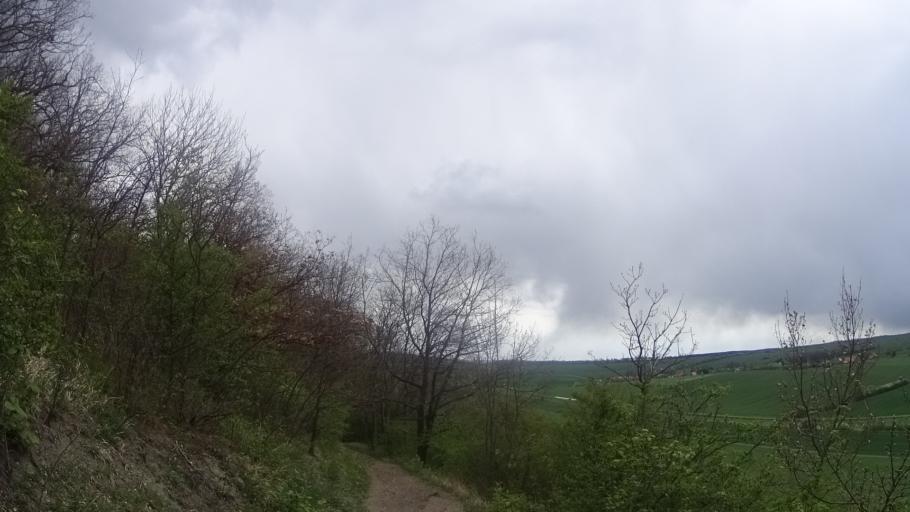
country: DE
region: Thuringia
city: Wandersleben
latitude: 50.8618
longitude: 10.8467
